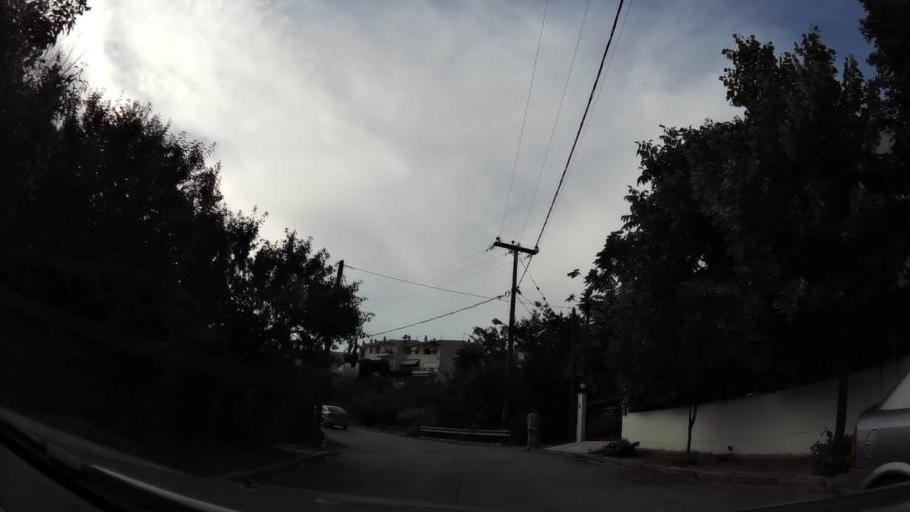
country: GR
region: Central Macedonia
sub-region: Nomos Thessalonikis
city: Pefka
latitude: 40.6565
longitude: 23.0018
